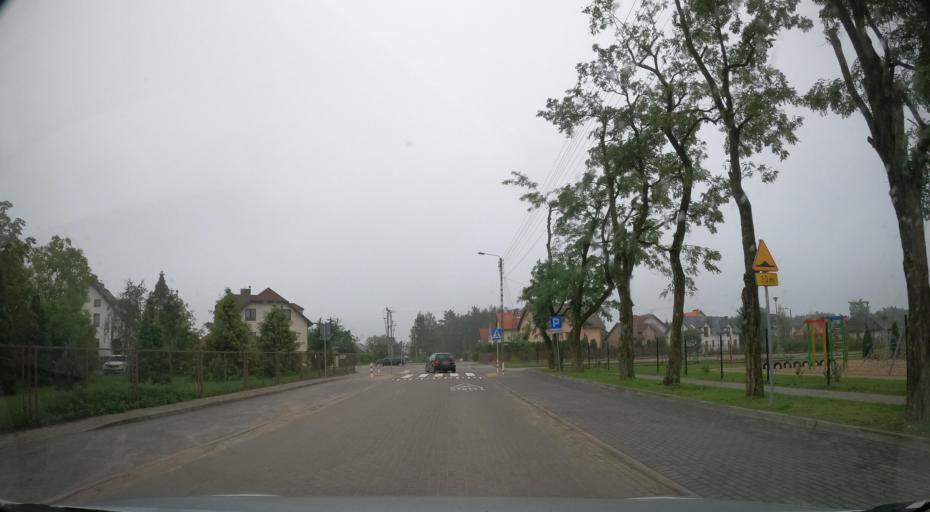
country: PL
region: Pomeranian Voivodeship
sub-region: Powiat kartuski
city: Chwaszczyno
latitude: 54.4397
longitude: 18.4184
